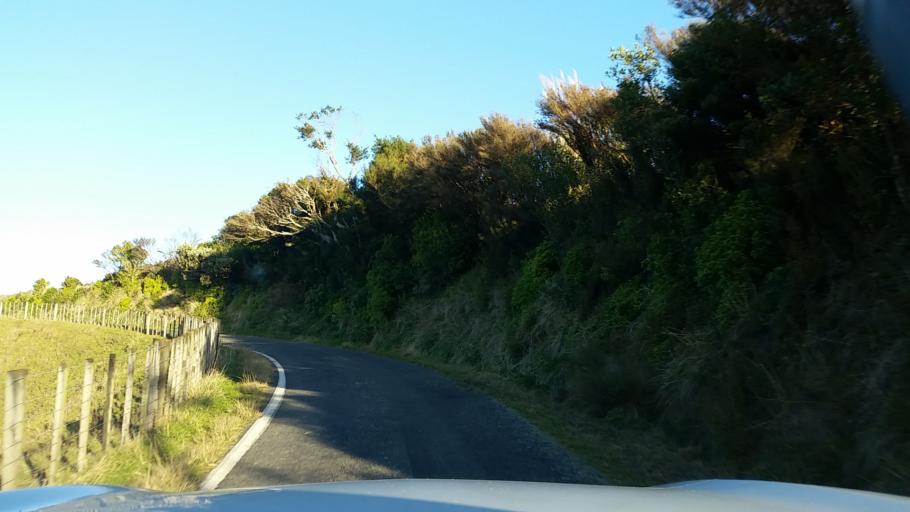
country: NZ
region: Taranaki
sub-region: South Taranaki District
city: Patea
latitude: -39.6321
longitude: 174.5205
